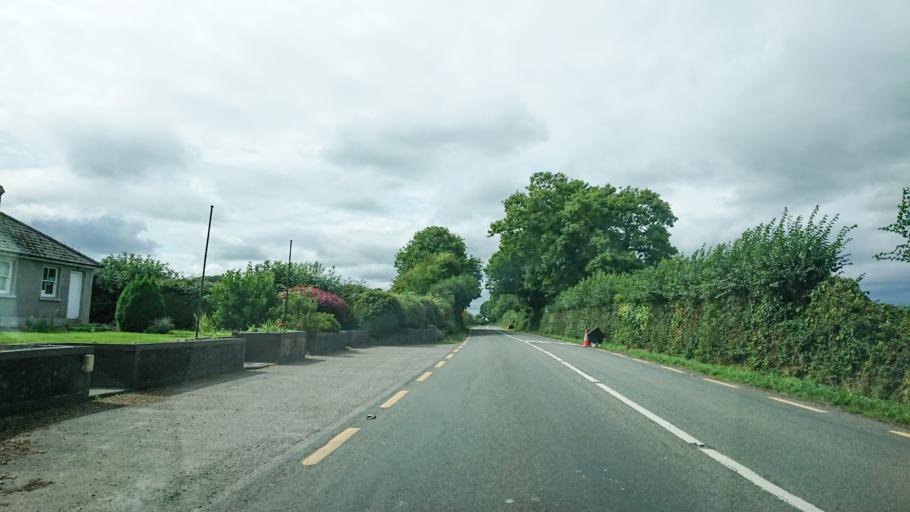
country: IE
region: Munster
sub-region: Waterford
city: Dungarvan
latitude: 52.1216
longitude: -7.7389
